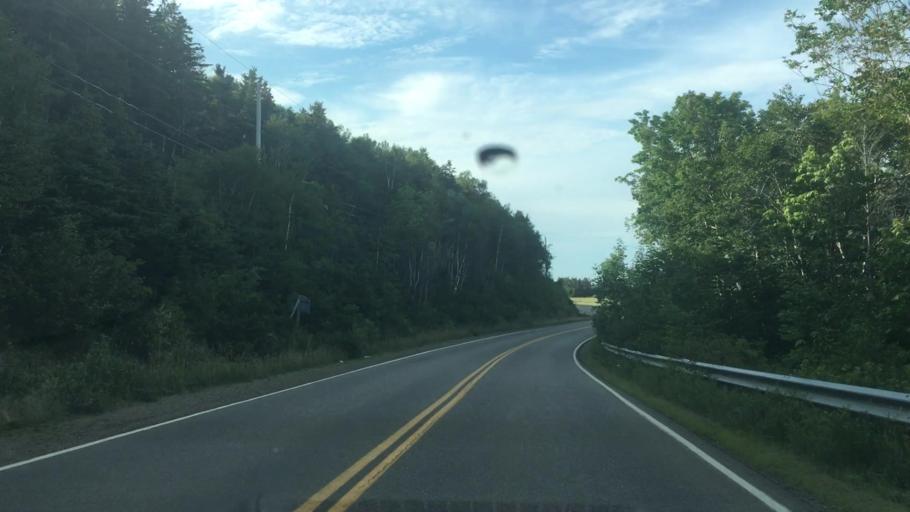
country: CA
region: Nova Scotia
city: Sydney Mines
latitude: 46.8250
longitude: -60.8010
